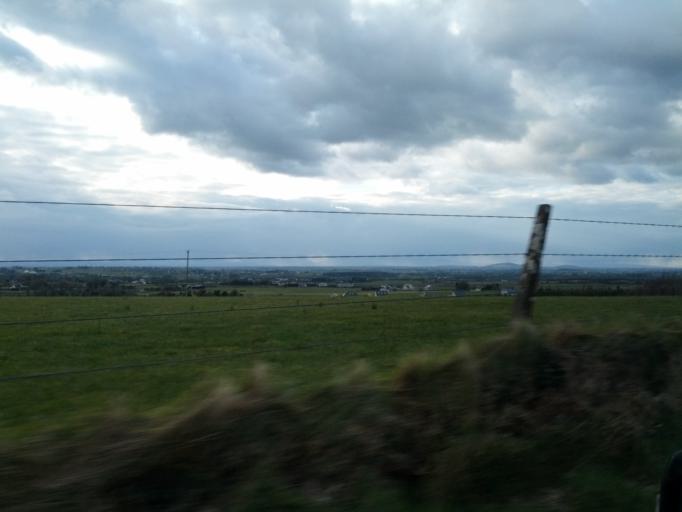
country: IE
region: Connaught
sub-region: County Galway
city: Athenry
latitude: 53.4089
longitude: -8.7511
